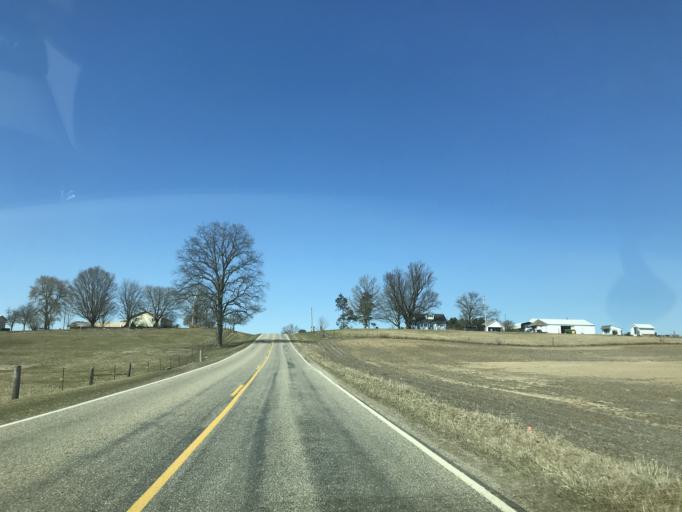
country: US
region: Michigan
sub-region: Hillsdale County
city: Jonesville
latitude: 41.9855
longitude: -84.7101
